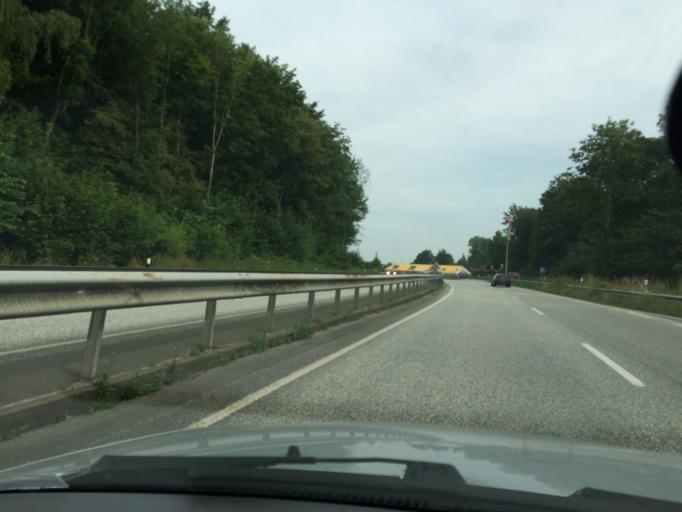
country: DK
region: South Denmark
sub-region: Aabenraa Kommune
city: Krusa
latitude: 54.8325
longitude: 9.4139
